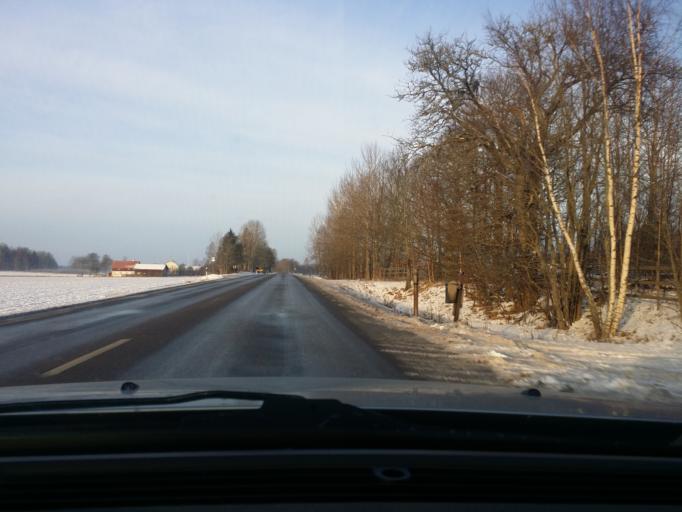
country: SE
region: OErebro
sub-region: Lindesbergs Kommun
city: Fellingsbro
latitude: 59.4628
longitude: 15.5627
